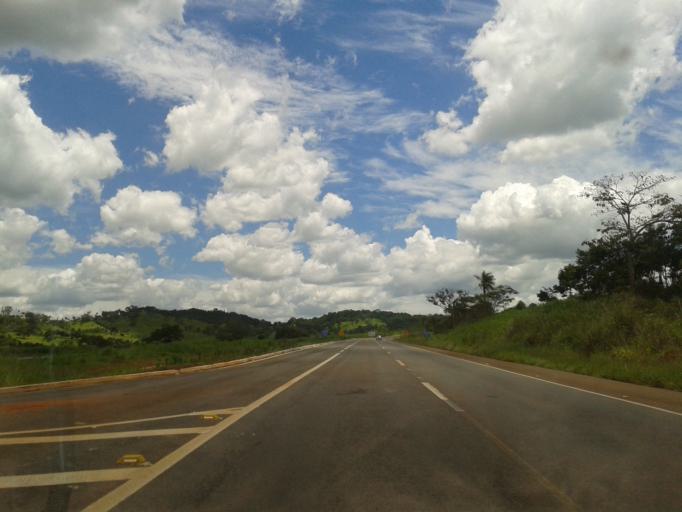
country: BR
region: Goias
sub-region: Neropolis
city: Neropolis
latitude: -16.2908
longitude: -49.2804
